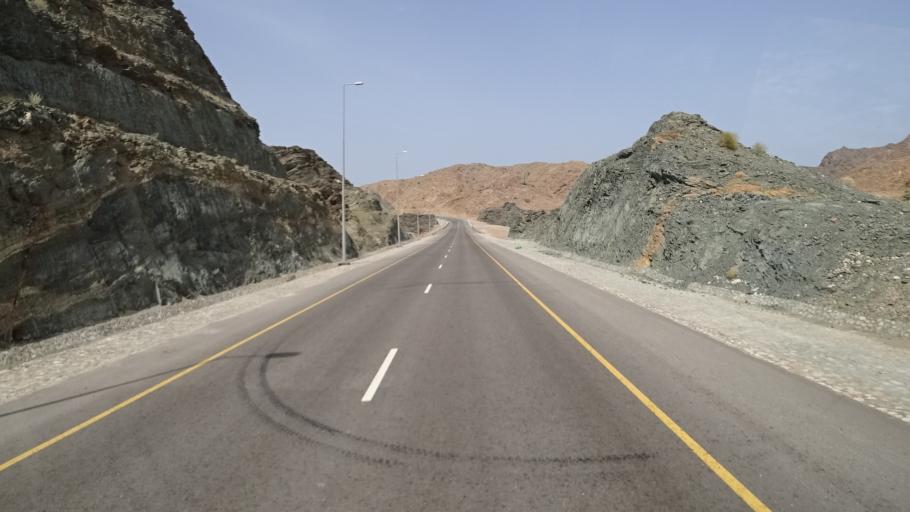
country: OM
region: Muhafazat Masqat
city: Muscat
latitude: 23.4554
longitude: 58.7579
